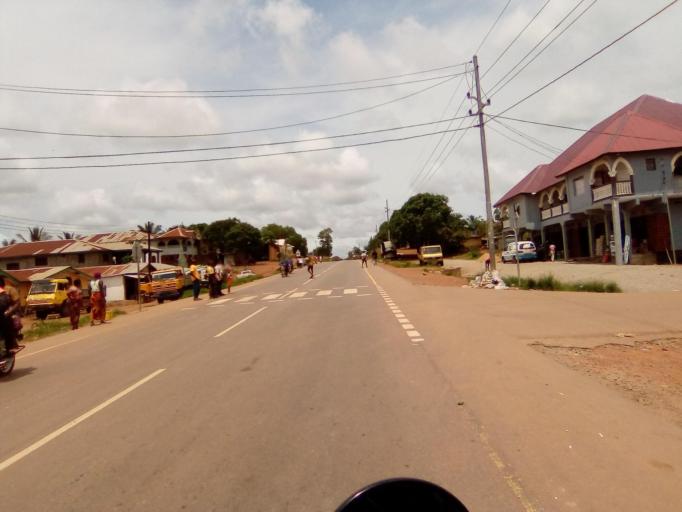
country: SL
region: Southern Province
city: Bo
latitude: 7.9338
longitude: -11.7253
